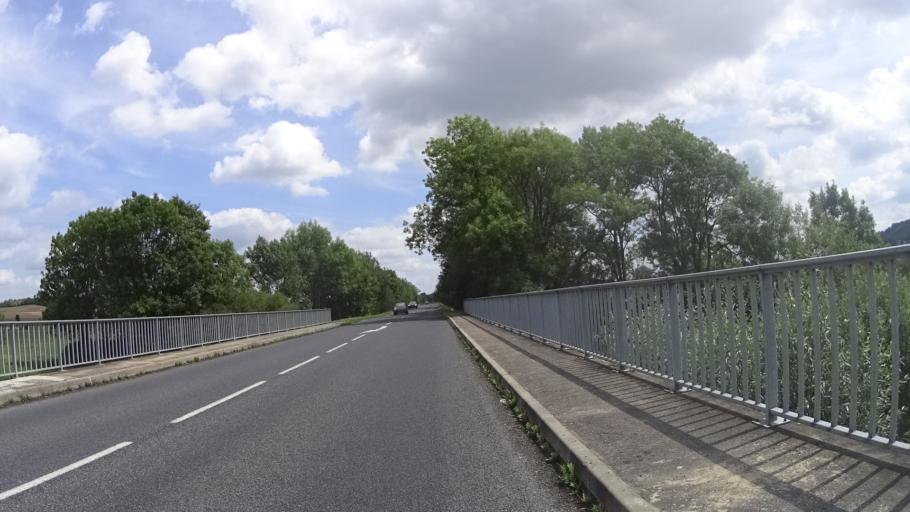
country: FR
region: Lorraine
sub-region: Departement de la Meuse
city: Euville
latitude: 48.7565
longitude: 5.6112
